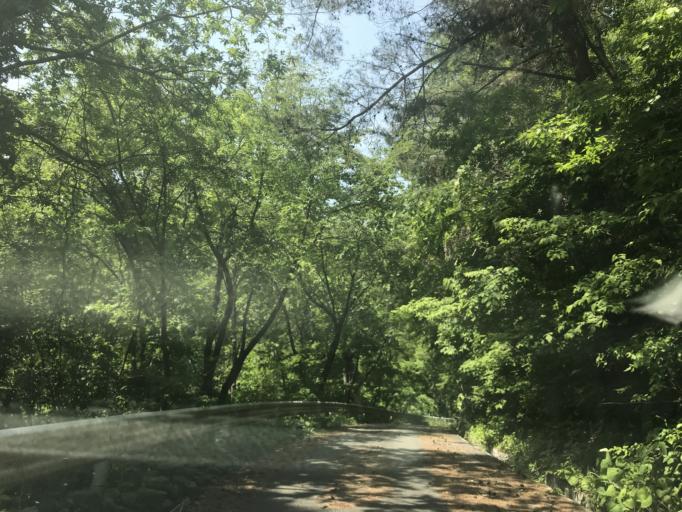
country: JP
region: Iwate
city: Ichinoseki
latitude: 38.9548
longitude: 141.2431
